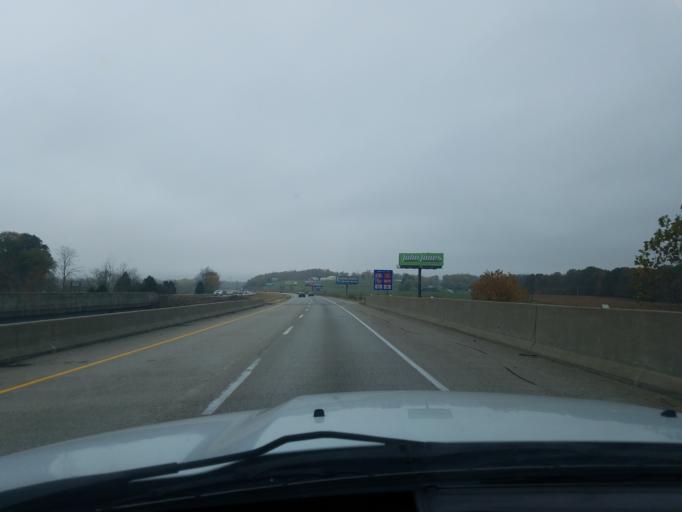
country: US
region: Indiana
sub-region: Harrison County
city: Corydon
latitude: 38.2436
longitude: -86.1025
